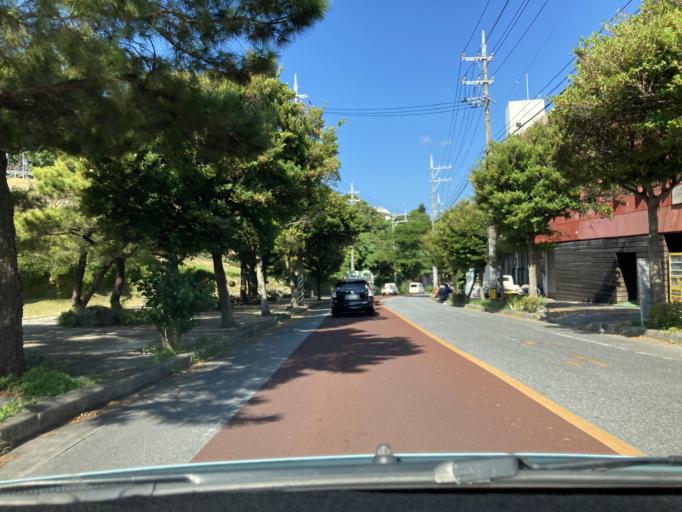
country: JP
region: Okinawa
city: Ginowan
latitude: 26.2583
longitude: 127.7238
